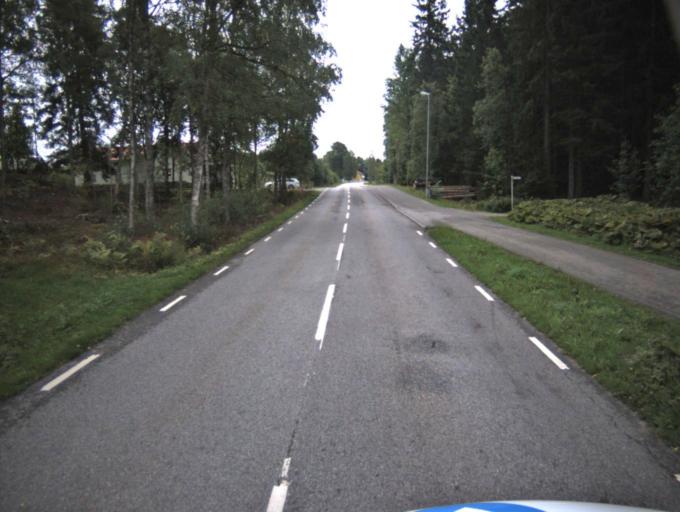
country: SE
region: Vaestra Goetaland
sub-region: Ulricehamns Kommun
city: Ulricehamn
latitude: 57.7759
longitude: 13.4299
